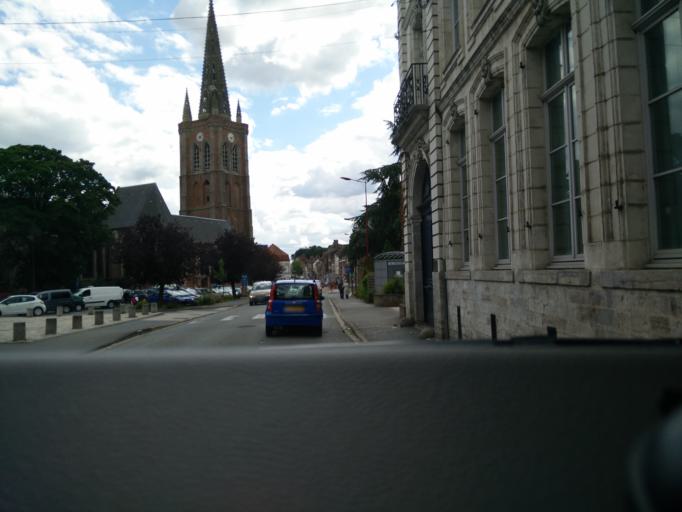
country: FR
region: Nord-Pas-de-Calais
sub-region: Departement du Nord
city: Hazebrouck
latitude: 50.7203
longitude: 2.5357
